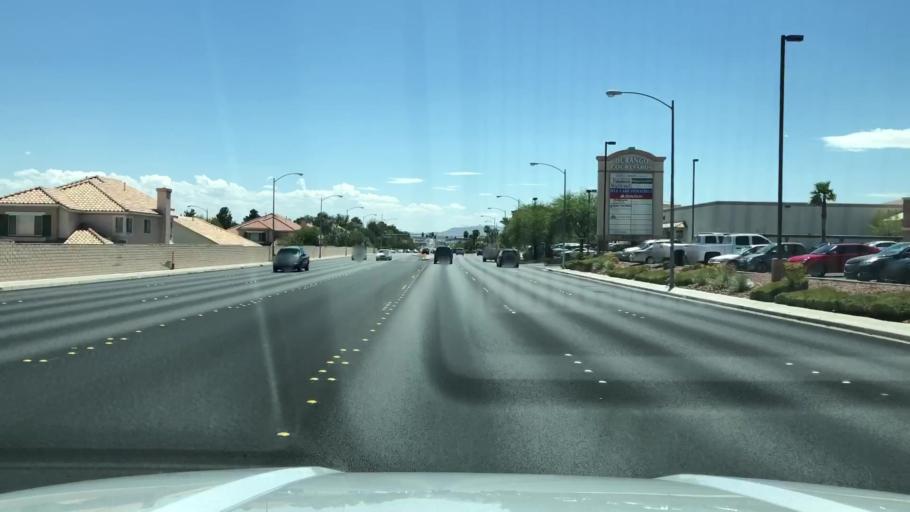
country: US
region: Nevada
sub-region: Clark County
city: Spring Valley
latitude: 36.1027
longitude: -115.2793
